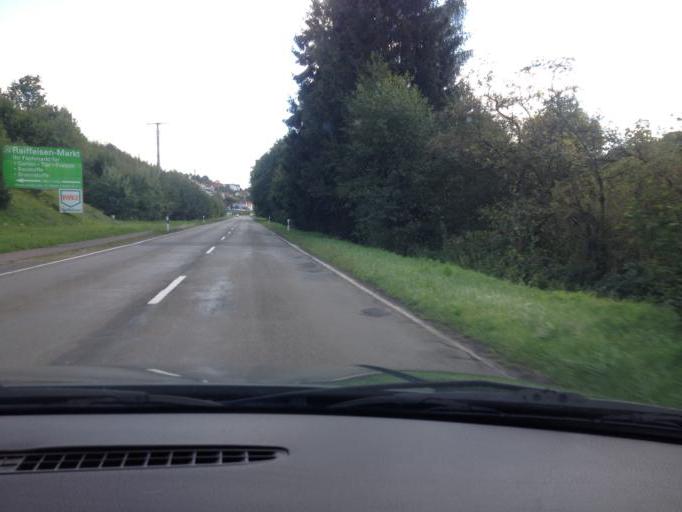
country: DE
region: Saarland
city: Marpingen
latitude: 49.4620
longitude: 7.0641
